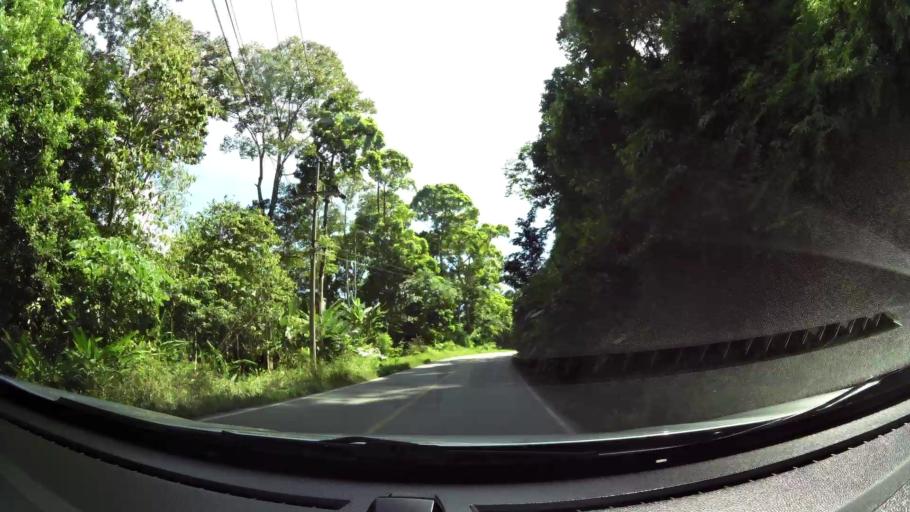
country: CR
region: San Jose
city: San Isidro
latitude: 9.2644
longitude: -83.8630
